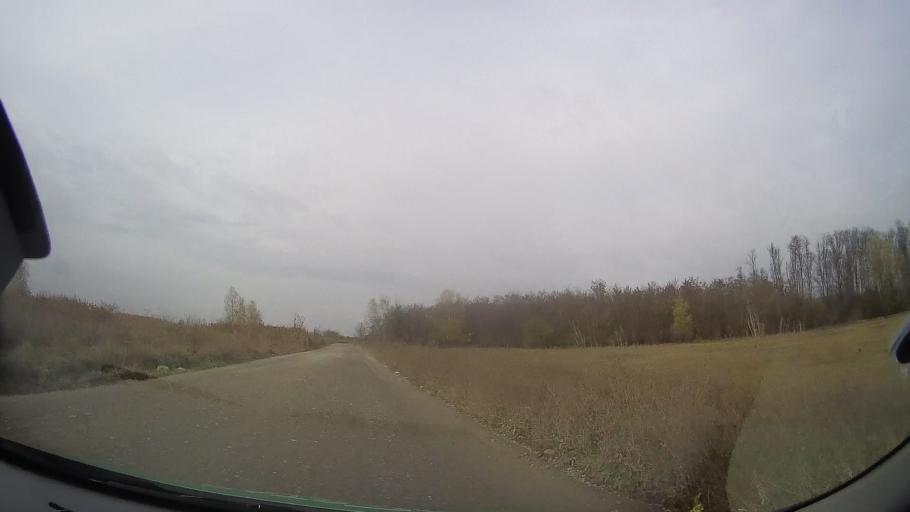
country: RO
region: Ialomita
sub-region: Comuna Fierbinti-Targ
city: Fierbinti-Targ
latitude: 44.6778
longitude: 26.3485
